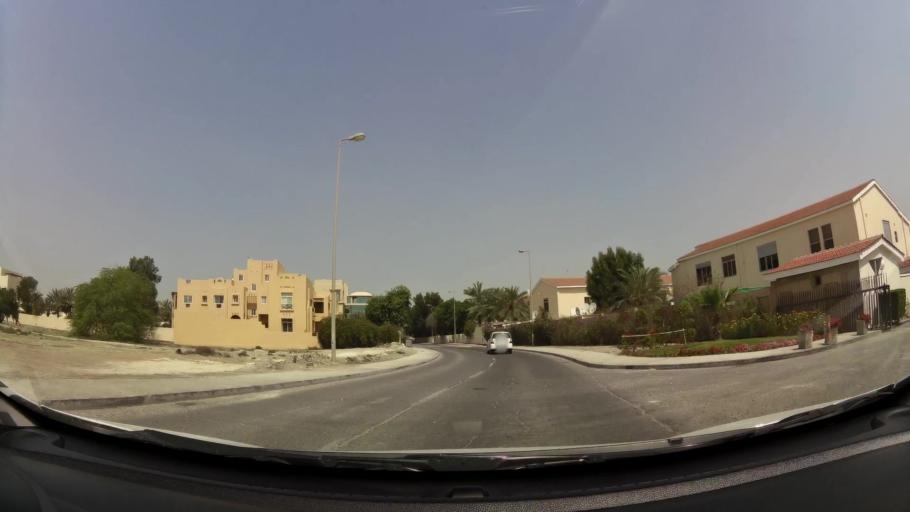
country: BH
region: Manama
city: Jidd Hafs
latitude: 26.2179
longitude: 50.4787
